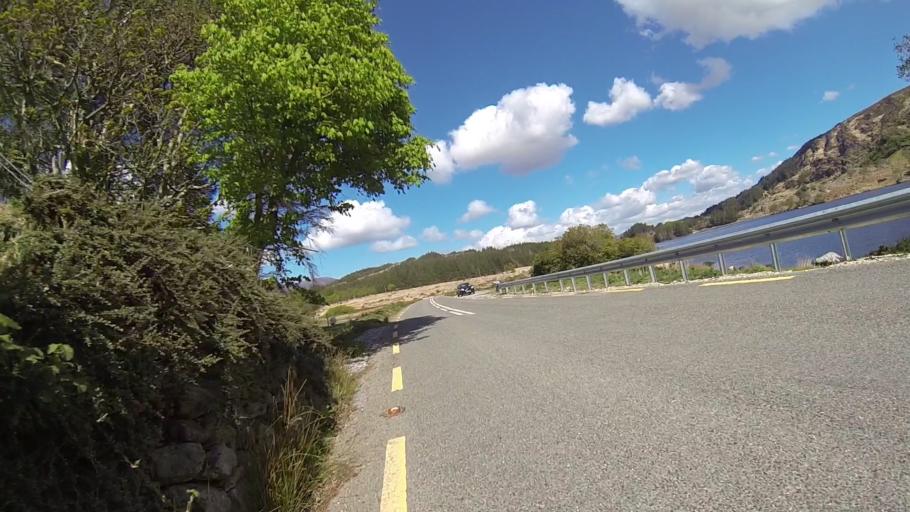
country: IE
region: Munster
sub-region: Ciarrai
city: Kenmare
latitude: 51.9562
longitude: -9.6225
